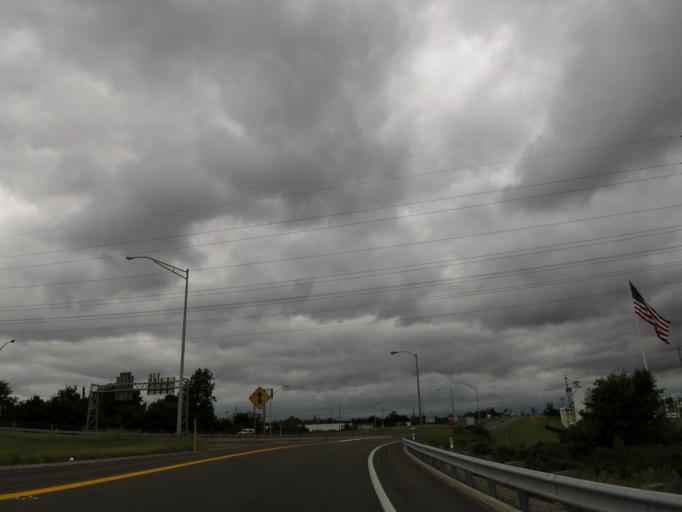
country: US
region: Kentucky
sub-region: McCracken County
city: Hendron
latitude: 37.0802
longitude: -88.6814
